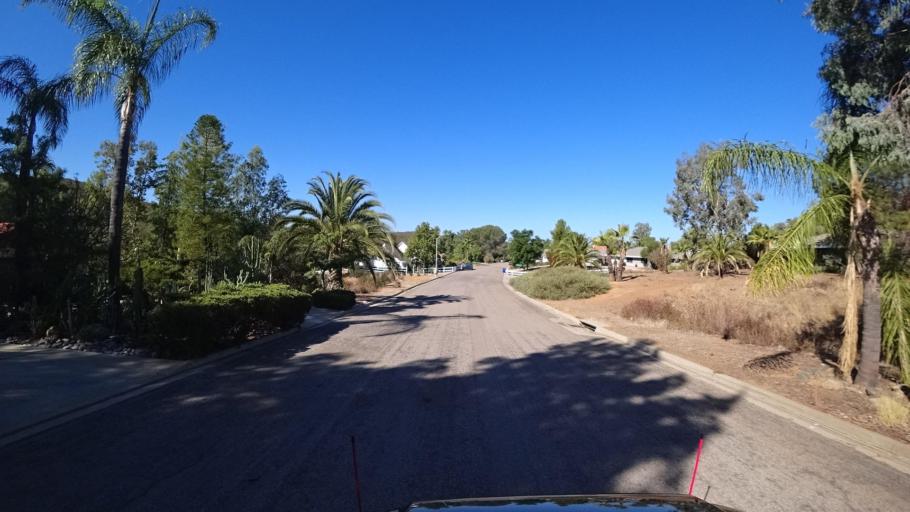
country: US
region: California
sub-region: San Diego County
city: San Diego Country Estates
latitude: 32.9998
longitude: -116.7621
